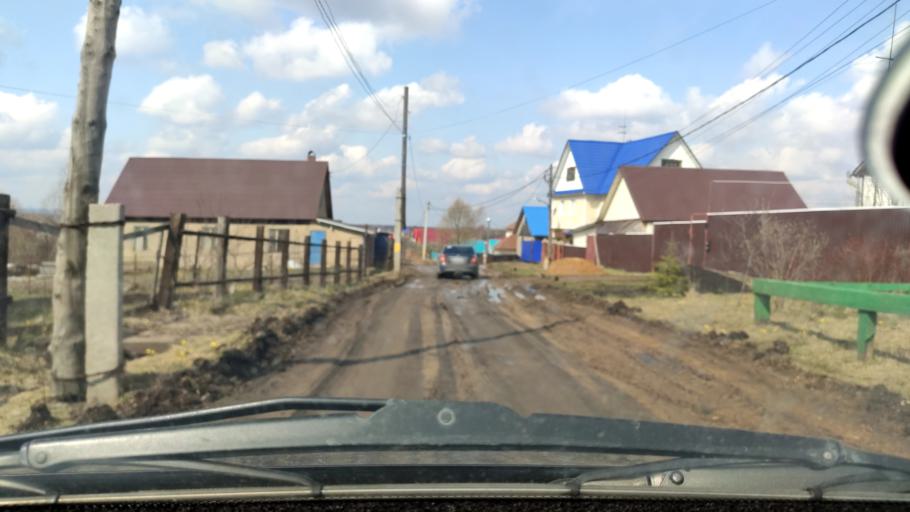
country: RU
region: Bashkortostan
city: Iglino
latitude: 54.8215
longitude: 56.3730
